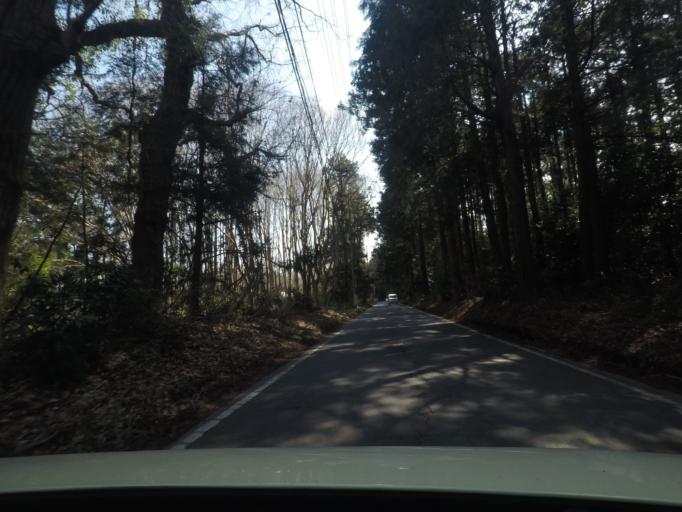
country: JP
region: Ibaraki
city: Ishioka
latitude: 36.1897
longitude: 140.3526
